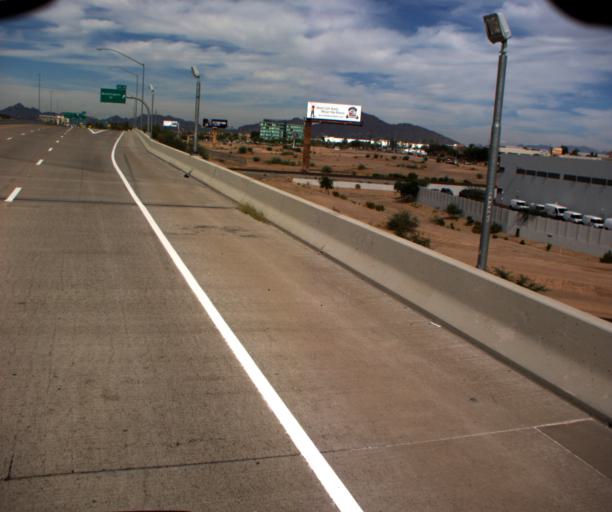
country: US
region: Arizona
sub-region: Maricopa County
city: Tempe Junction
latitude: 33.4423
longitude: -111.9802
